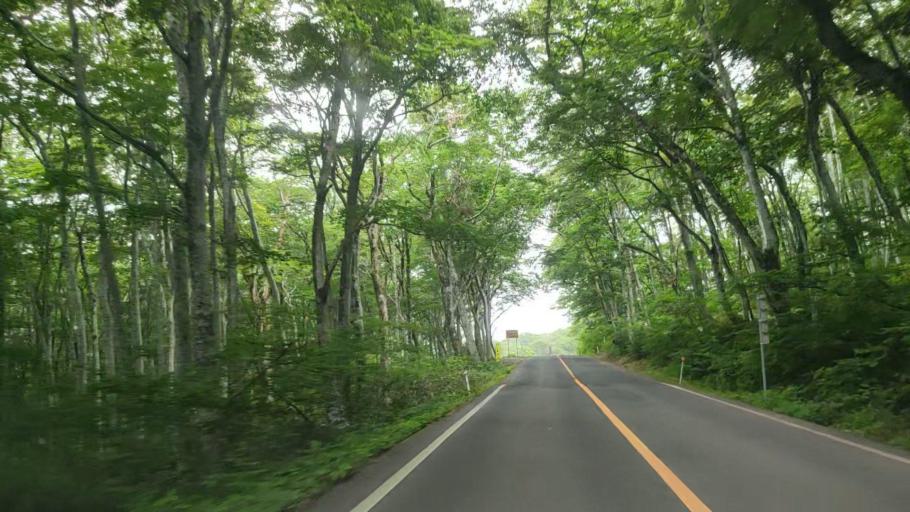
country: JP
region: Tottori
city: Yonago
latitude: 35.3544
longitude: 133.5390
